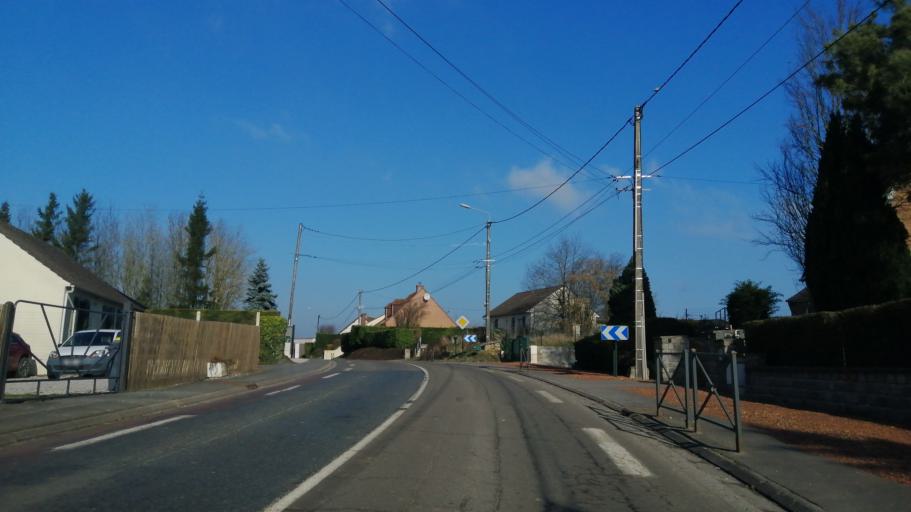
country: FR
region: Nord-Pas-de-Calais
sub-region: Departement du Pas-de-Calais
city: Aubigny-en-Artois
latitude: 50.3787
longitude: 2.6330
